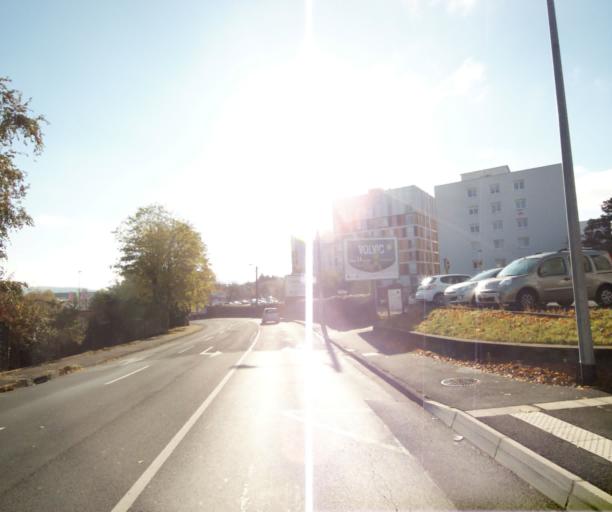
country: FR
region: Auvergne
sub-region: Departement du Puy-de-Dome
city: Aubiere
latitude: 45.7658
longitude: 3.1217
